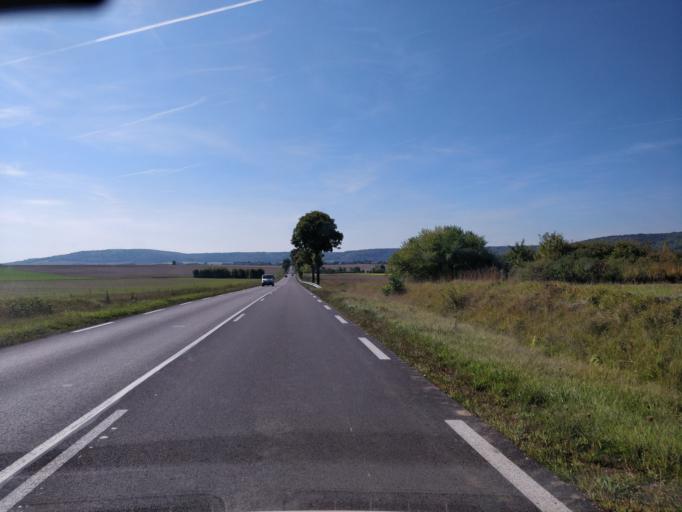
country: FR
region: Champagne-Ardenne
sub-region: Departement de l'Aube
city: Bouilly
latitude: 48.2152
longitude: 4.0096
